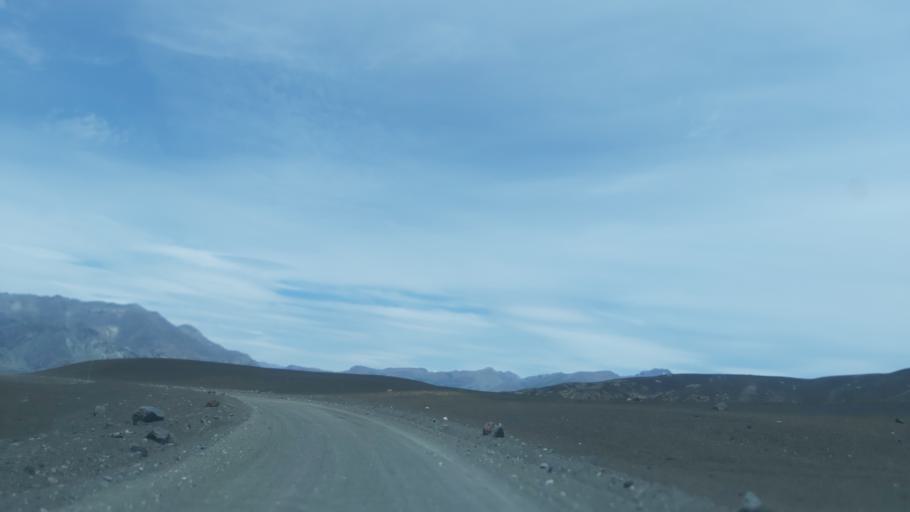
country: AR
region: Neuquen
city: Andacollo
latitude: -37.4202
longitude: -71.2891
